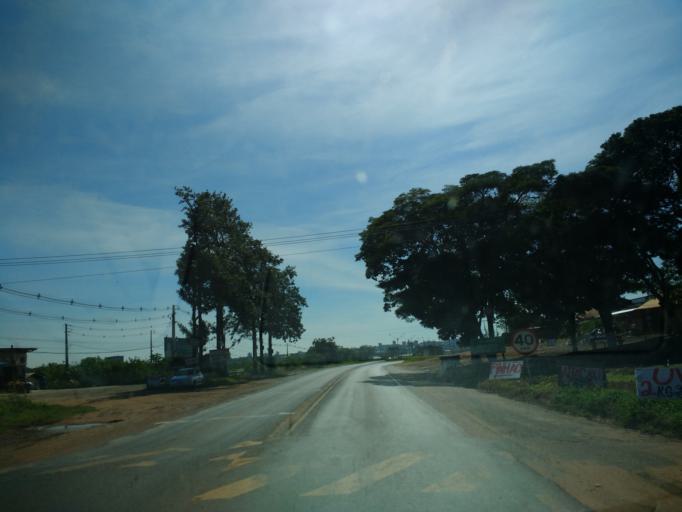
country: BR
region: Parana
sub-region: Umuarama
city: Umuarama
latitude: -23.7924
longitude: -53.3158
